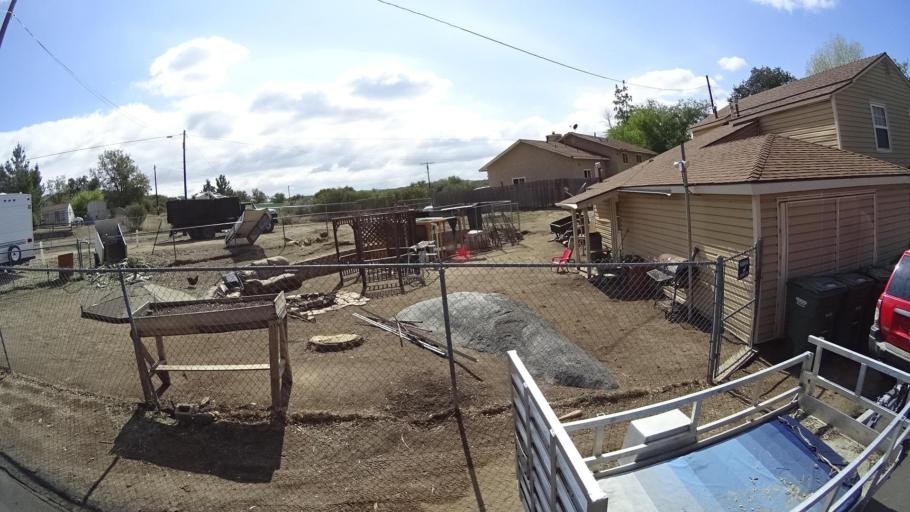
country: US
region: California
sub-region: San Diego County
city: Campo
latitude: 32.6783
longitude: -116.5038
